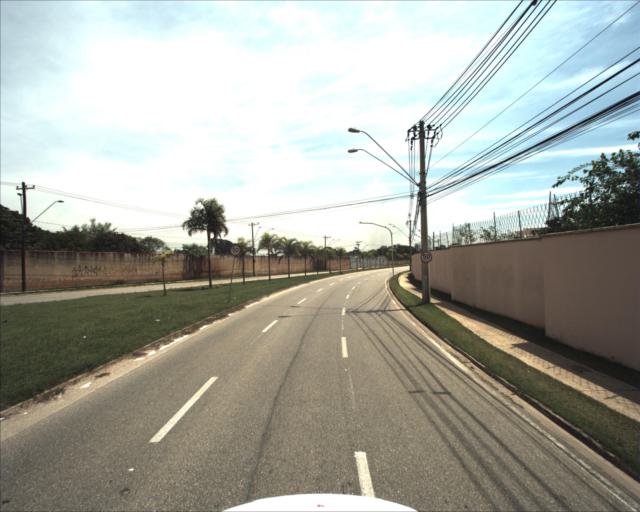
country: BR
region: Sao Paulo
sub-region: Votorantim
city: Votorantim
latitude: -23.5483
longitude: -47.4770
